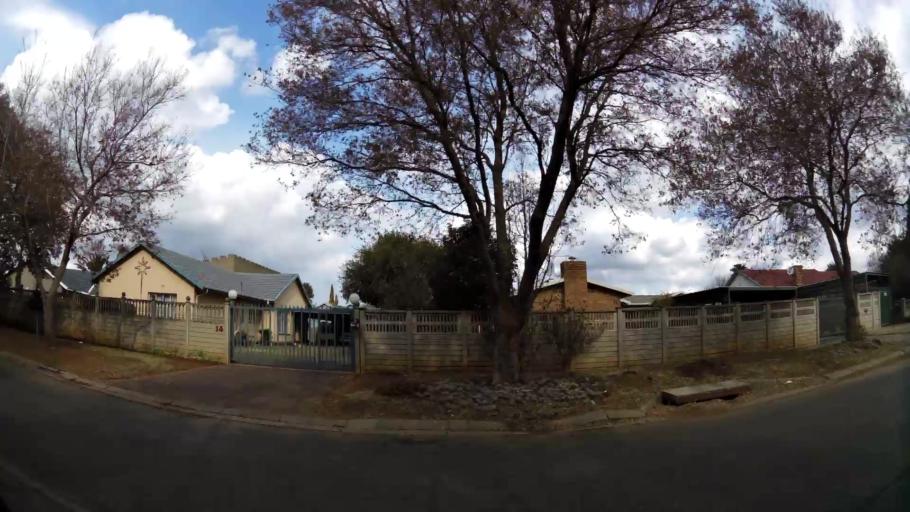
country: ZA
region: Gauteng
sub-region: Sedibeng District Municipality
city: Vanderbijlpark
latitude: -26.7248
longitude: 27.8506
